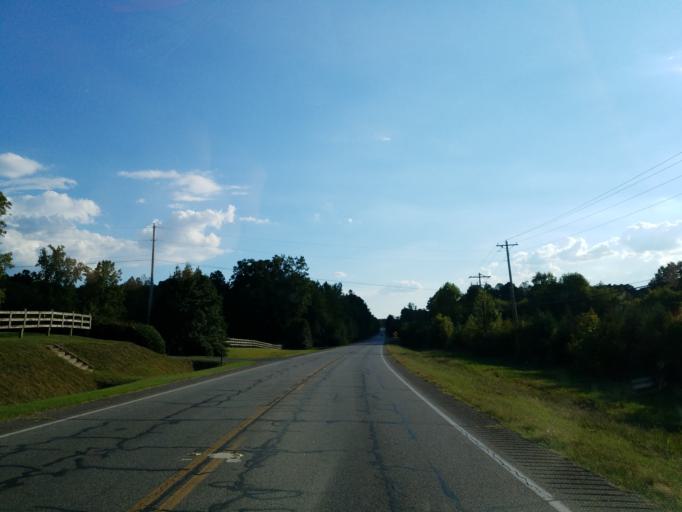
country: US
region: Tennessee
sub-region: Bradley County
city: Wildwood Lake
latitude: 34.9497
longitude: -84.7375
